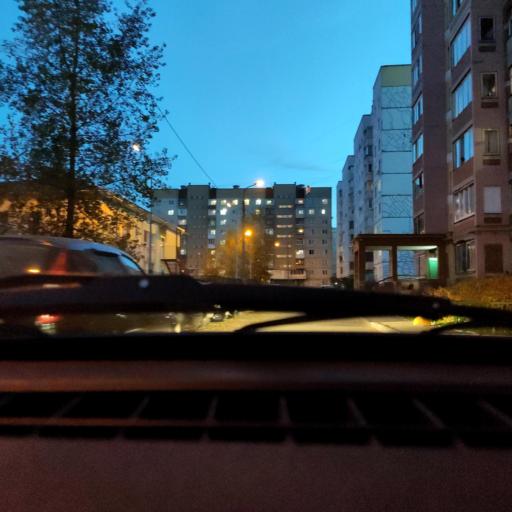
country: RU
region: Bashkortostan
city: Ufa
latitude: 54.7838
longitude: 56.1093
